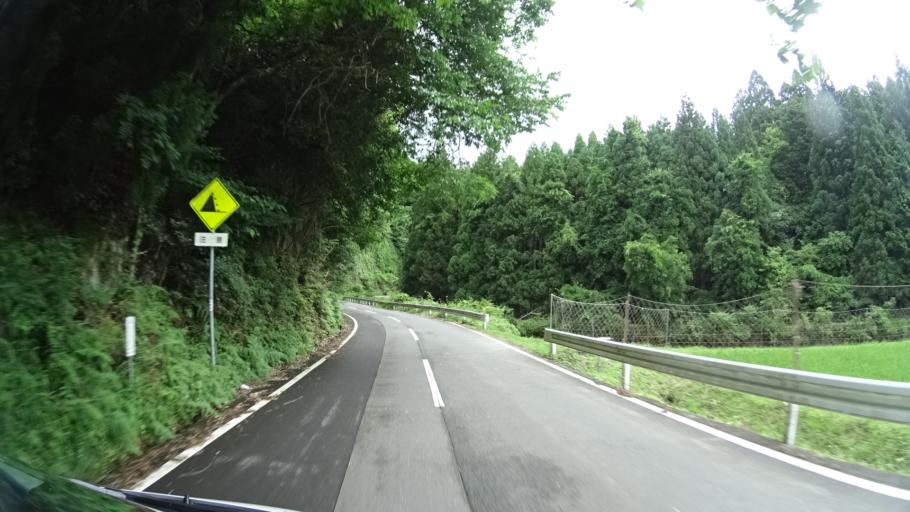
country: JP
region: Hyogo
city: Sasayama
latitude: 35.0654
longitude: 135.3989
